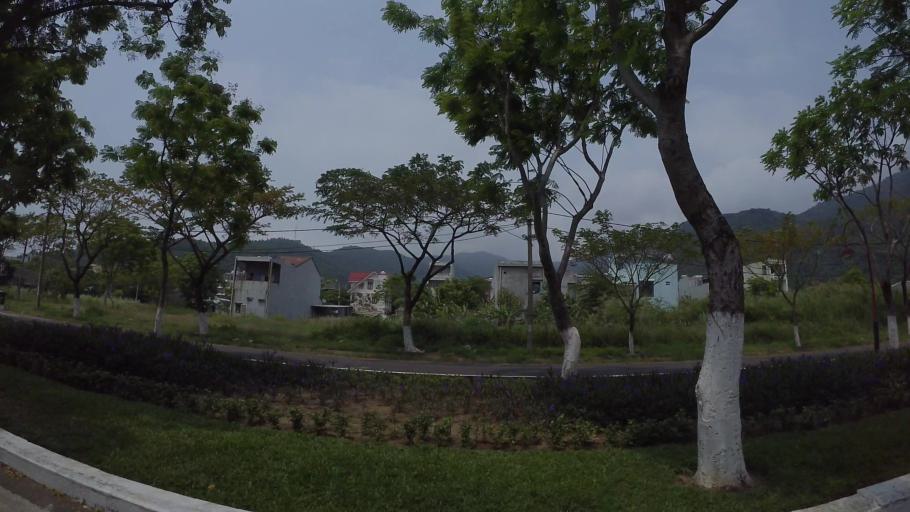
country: VN
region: Da Nang
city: Son Tra
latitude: 16.1059
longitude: 108.2607
